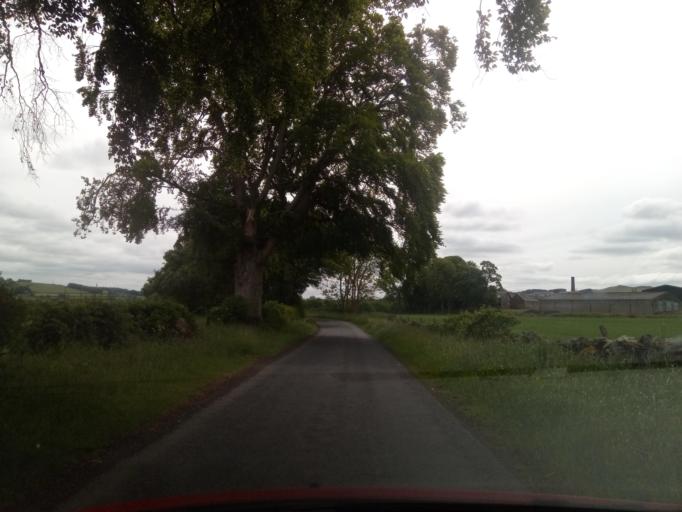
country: GB
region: Scotland
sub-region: The Scottish Borders
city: Galashiels
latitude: 55.5838
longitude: -2.8190
